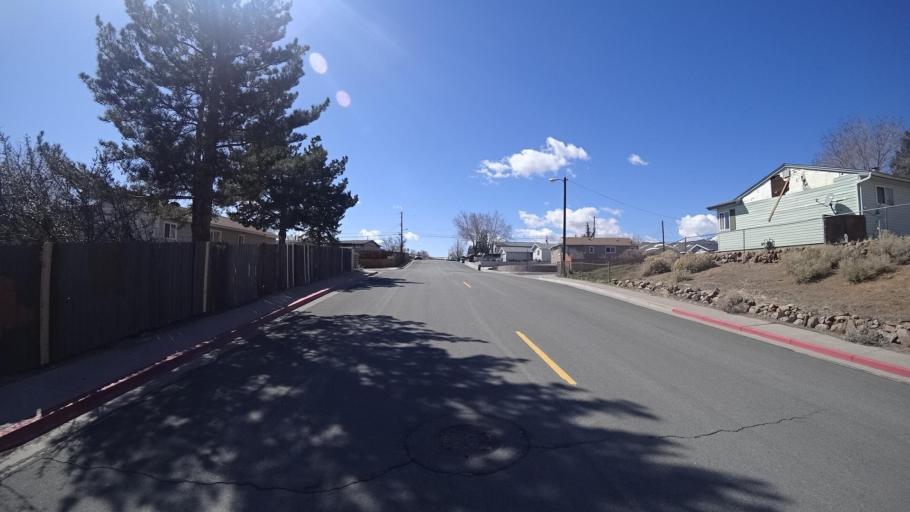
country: US
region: Nevada
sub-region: Washoe County
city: Golden Valley
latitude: 39.5920
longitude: -119.8391
